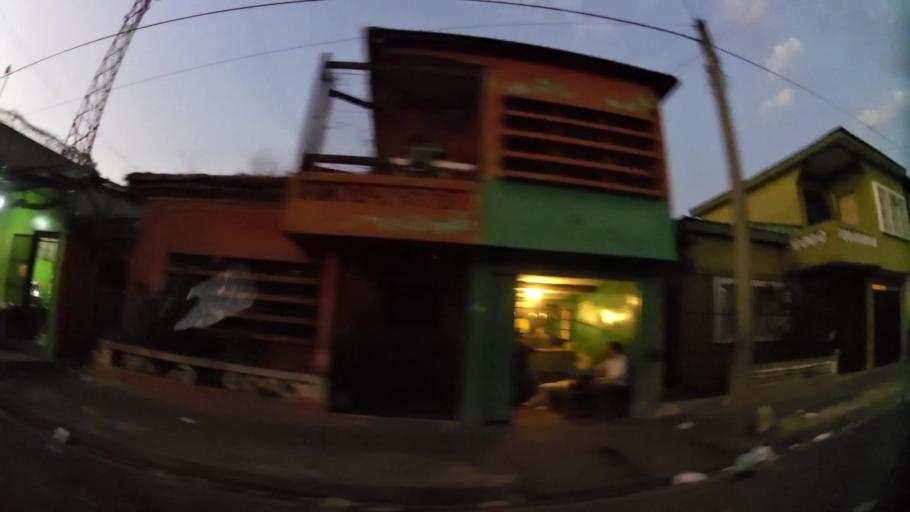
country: SV
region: San Salvador
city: San Salvador
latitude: 13.7085
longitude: -89.1890
